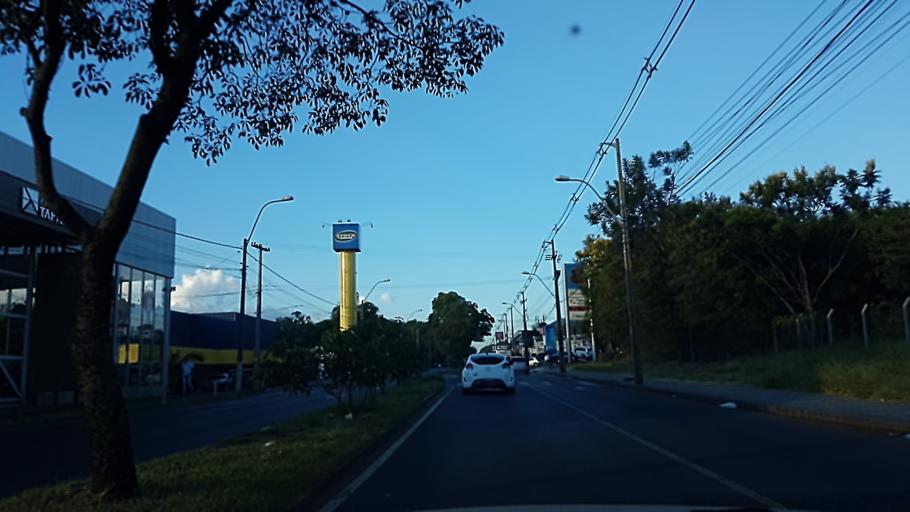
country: PY
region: Asuncion
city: Asuncion
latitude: -25.2684
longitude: -57.5832
